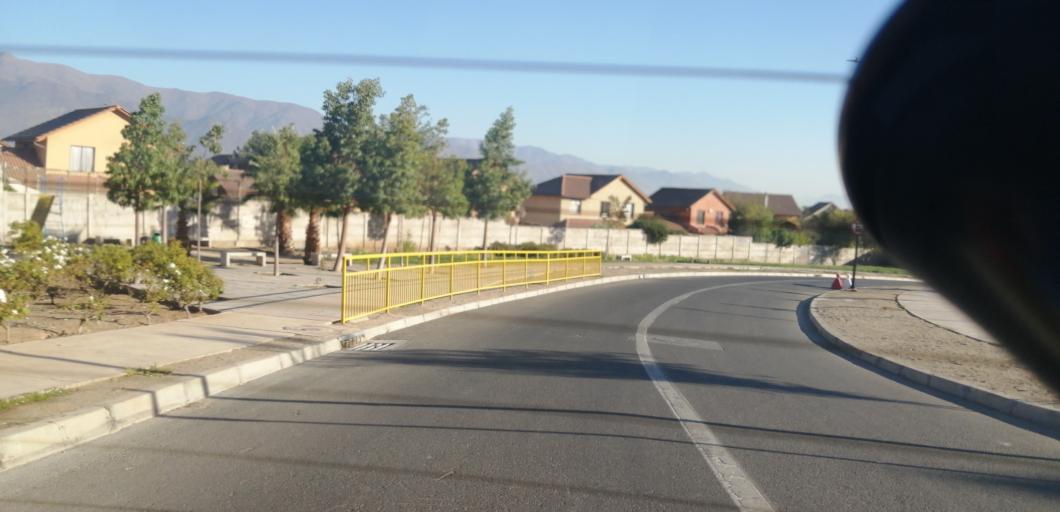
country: CL
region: Santiago Metropolitan
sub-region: Provincia de Santiago
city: Lo Prado
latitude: -33.4529
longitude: -70.8450
